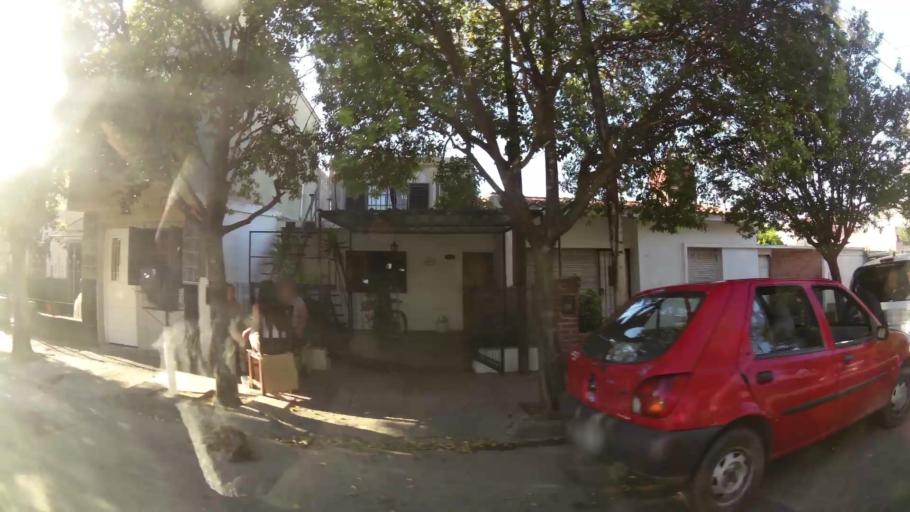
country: AR
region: Cordoba
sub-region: Departamento de Capital
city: Cordoba
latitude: -31.3786
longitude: -64.1805
